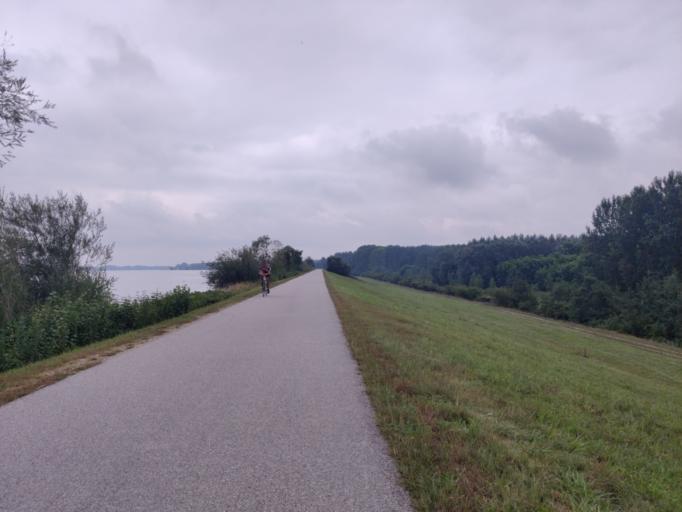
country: AT
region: Lower Austria
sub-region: Politischer Bezirk Tulln
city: Grafenworth
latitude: 48.3787
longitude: 15.8049
